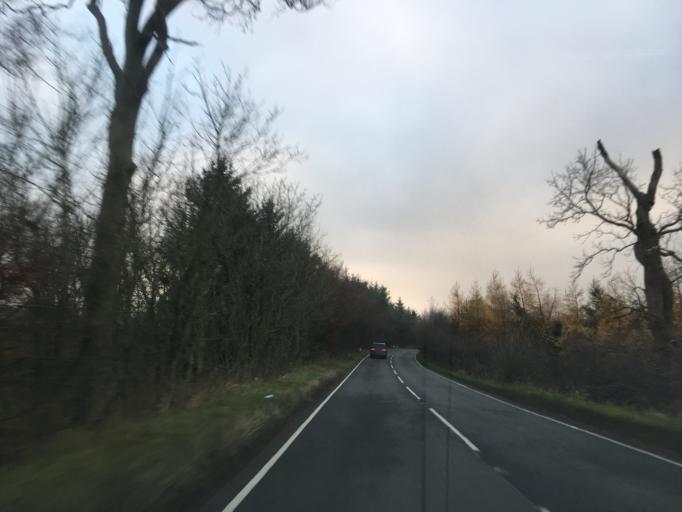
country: GB
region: Scotland
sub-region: Fife
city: Strathkinness
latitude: 56.2799
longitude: -2.8406
